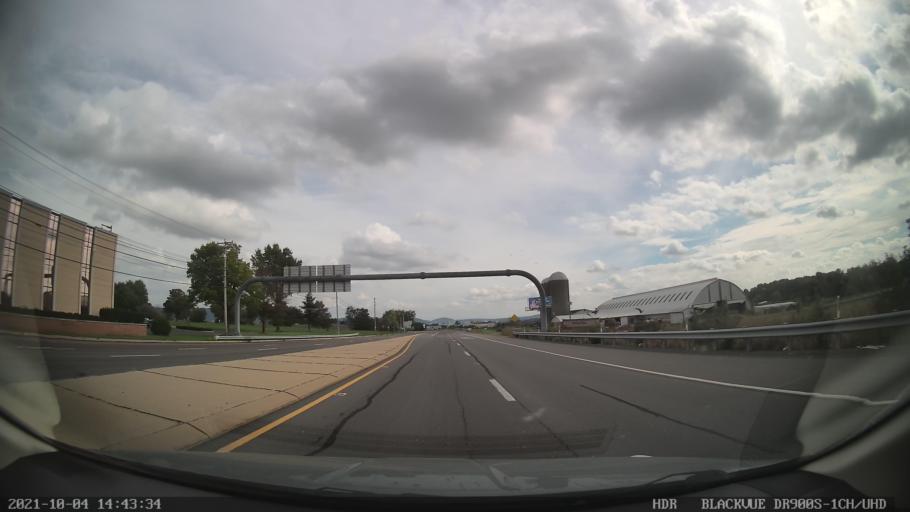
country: US
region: Pennsylvania
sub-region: Berks County
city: Fox Chase
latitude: 40.3802
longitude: -75.9833
